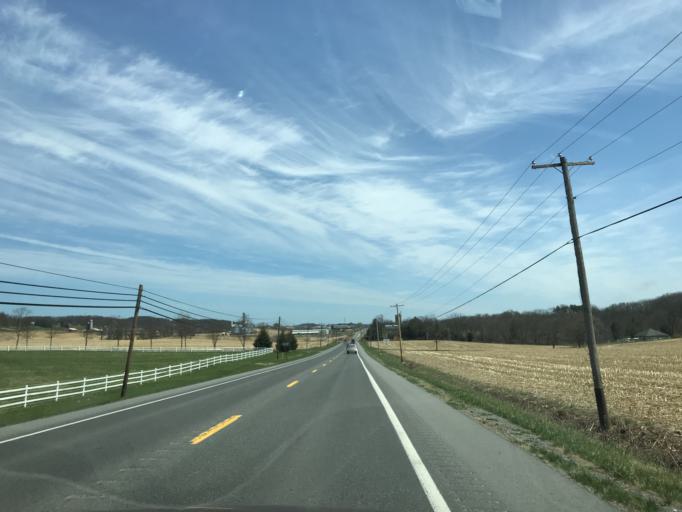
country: US
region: Pennsylvania
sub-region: Snyder County
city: Selinsgrove
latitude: 40.8064
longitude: -76.9312
